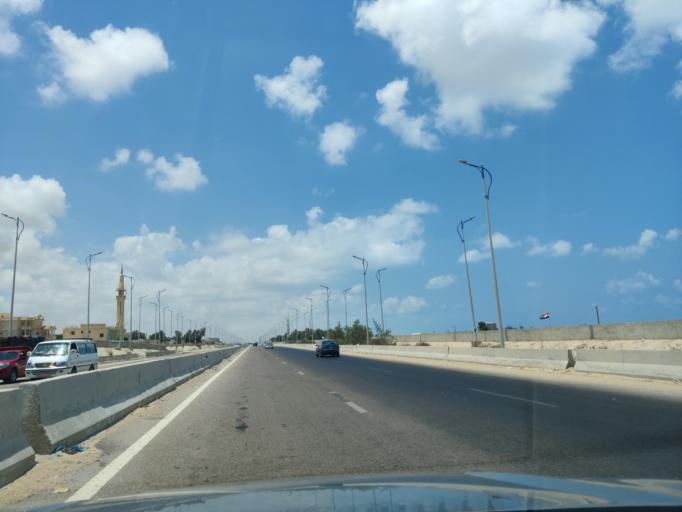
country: EG
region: Alexandria
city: Alexandria
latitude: 30.9551
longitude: 29.5321
